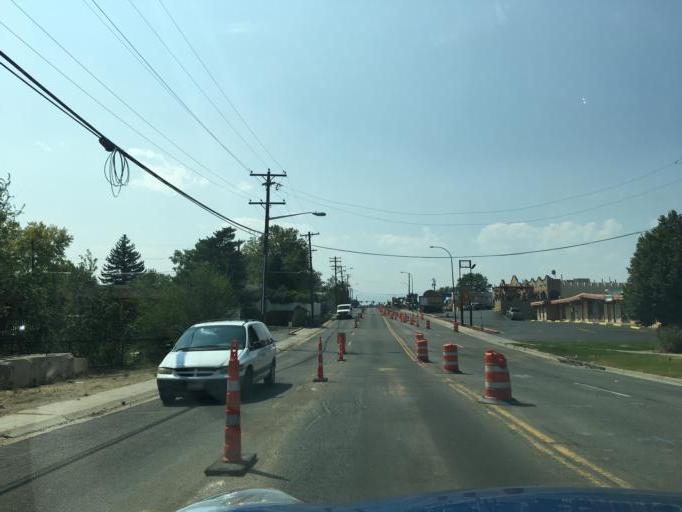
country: US
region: Colorado
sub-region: Adams County
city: Westminster
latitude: 39.8418
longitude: -105.0487
